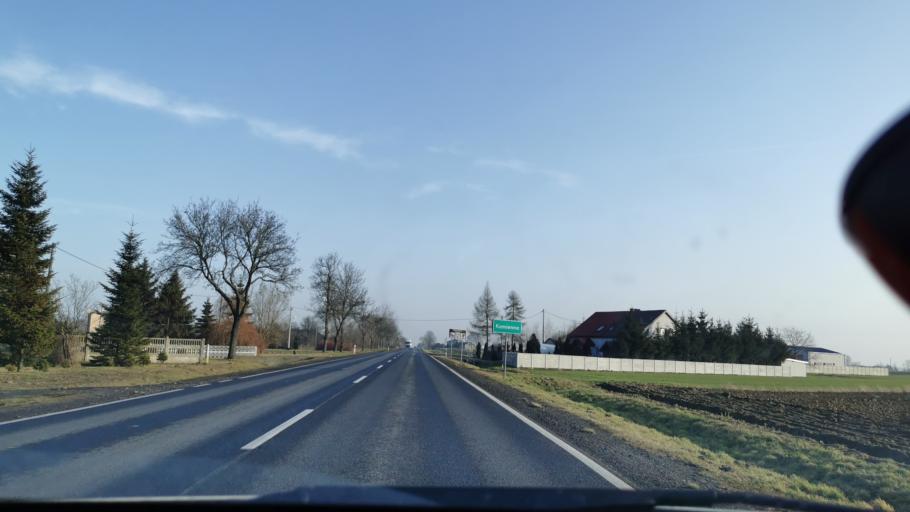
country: PL
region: Lodz Voivodeship
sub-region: Powiat sieradzki
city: Blaszki
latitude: 51.6748
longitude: 18.3604
